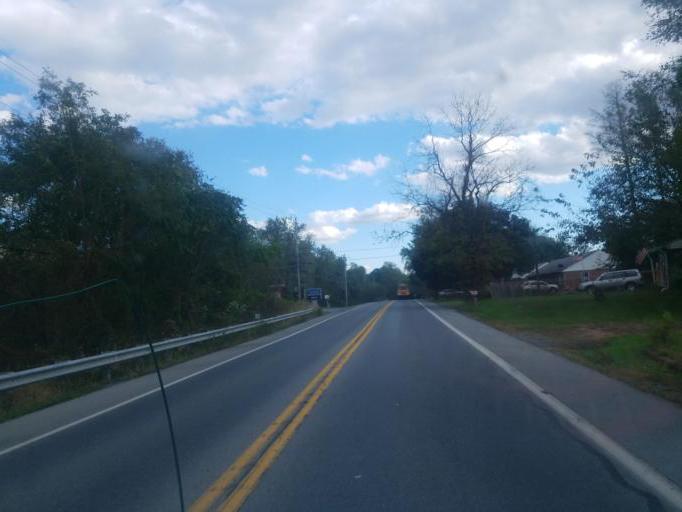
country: US
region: Pennsylvania
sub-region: Dauphin County
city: Middletown
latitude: 40.1686
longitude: -76.7216
